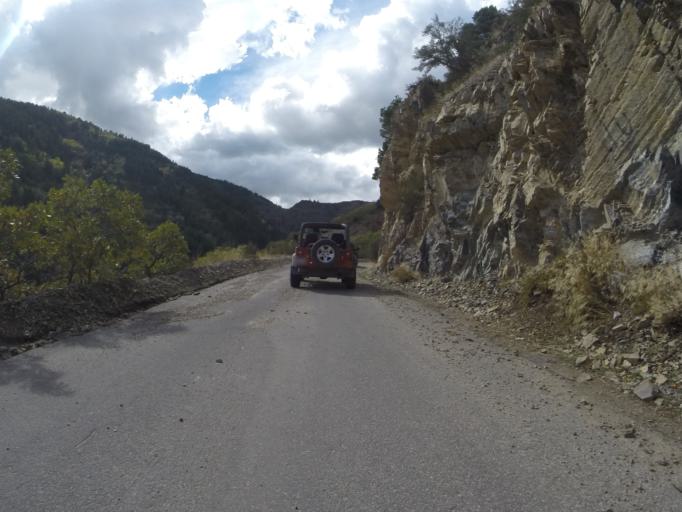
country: US
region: Utah
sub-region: Salt Lake County
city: Herriman
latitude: 40.4876
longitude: -112.1603
